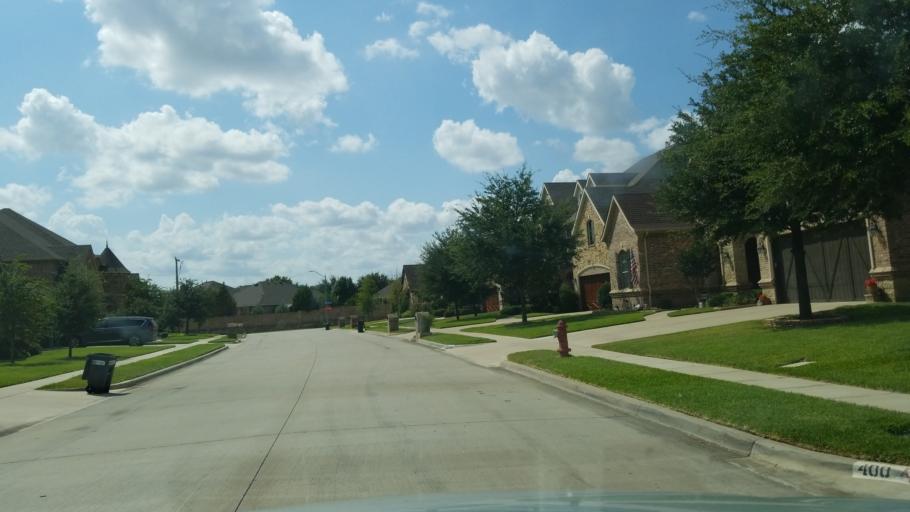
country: US
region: Texas
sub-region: Tarrant County
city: Euless
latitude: 32.8696
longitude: -97.0873
